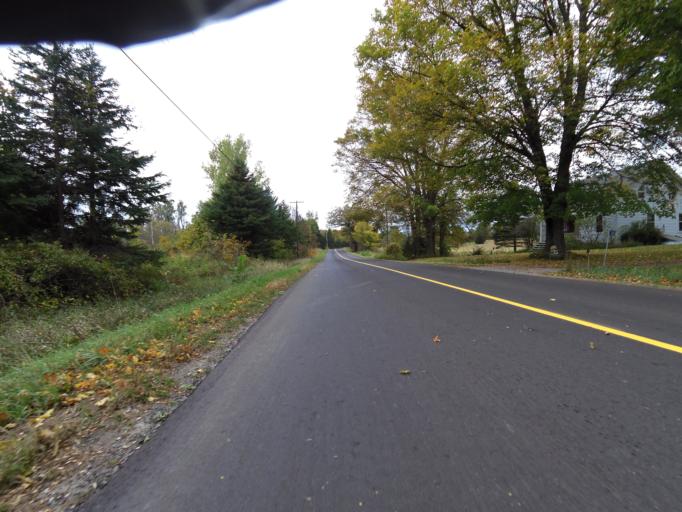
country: CA
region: Ontario
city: Gananoque
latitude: 44.5816
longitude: -76.0597
